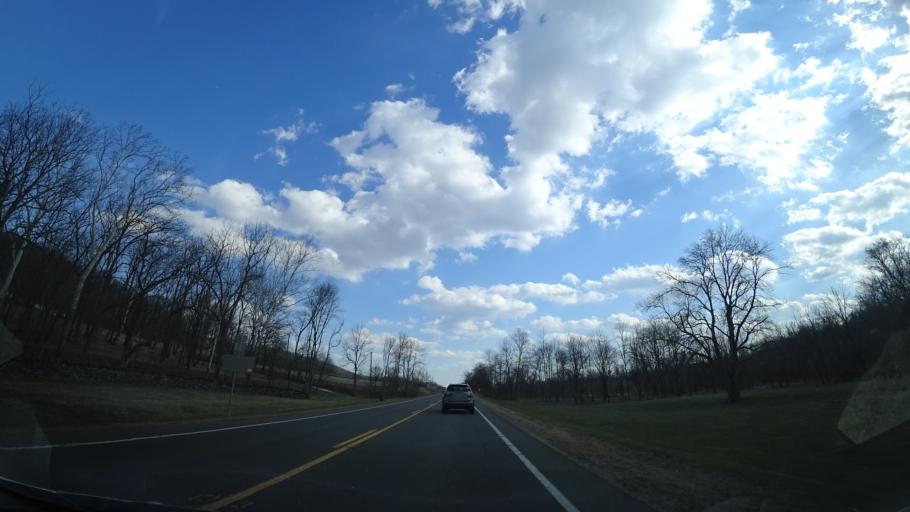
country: US
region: Virginia
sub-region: Fauquier County
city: Marshall
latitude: 38.9536
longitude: -77.9409
